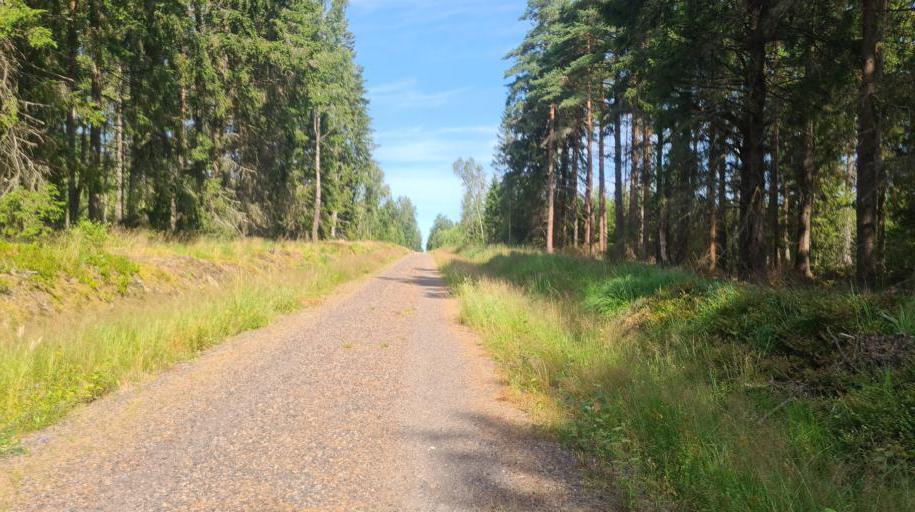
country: SE
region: Kronoberg
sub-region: Ljungby Kommun
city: Lagan
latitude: 56.9598
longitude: 13.9558
